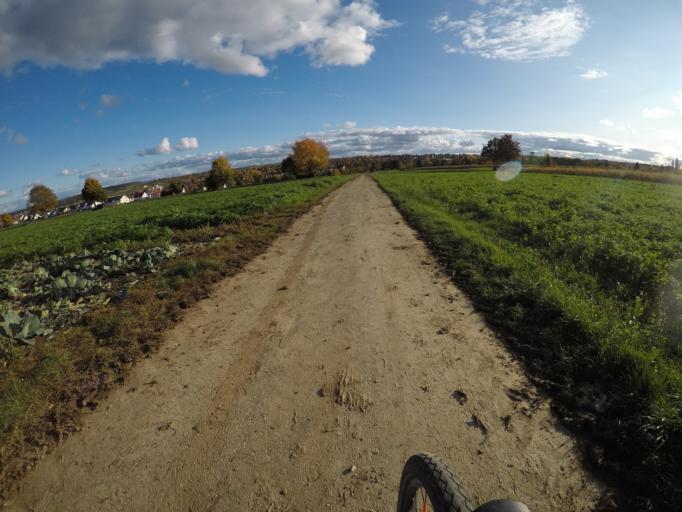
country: DE
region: Baden-Wuerttemberg
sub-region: Regierungsbezirk Stuttgart
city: Filderstadt
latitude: 48.6803
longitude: 9.2326
